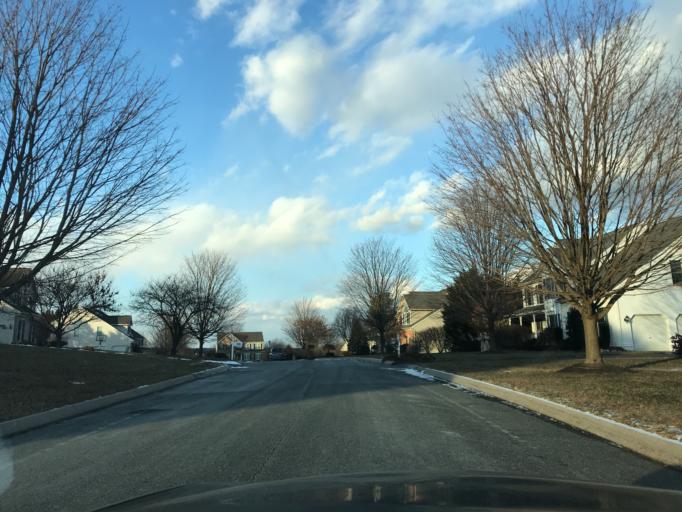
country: US
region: Maryland
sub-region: Harford County
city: Bel Air North
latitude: 39.5866
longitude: -76.3774
